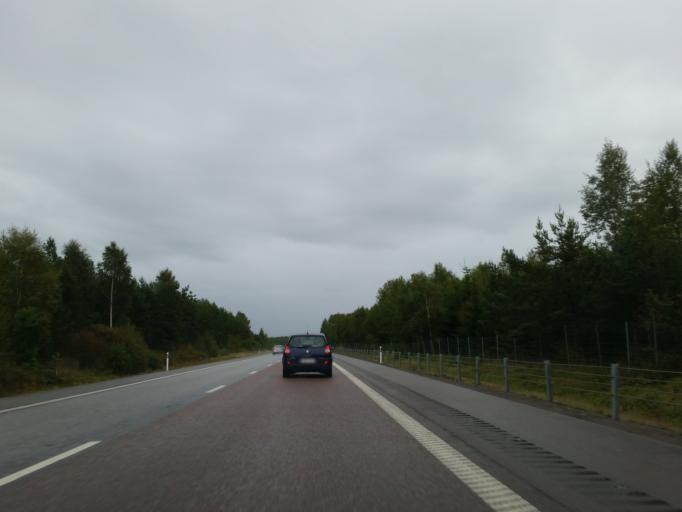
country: SE
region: Uppsala
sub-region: Enkopings Kommun
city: Dalby
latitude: 59.6097
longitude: 17.4175
